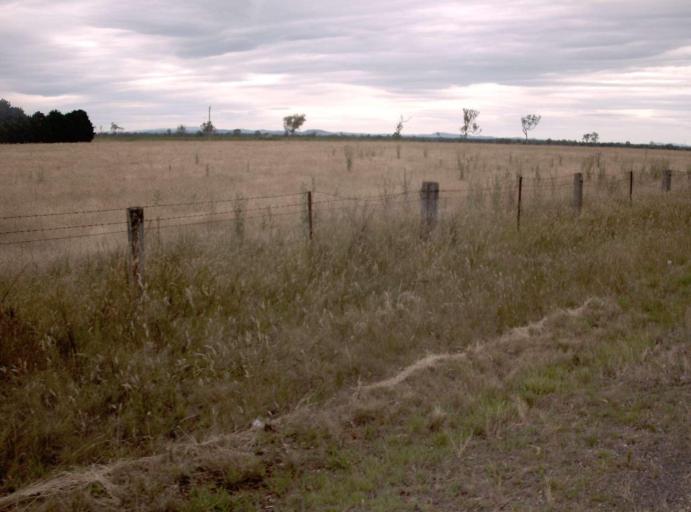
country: AU
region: Victoria
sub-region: East Gippsland
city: Bairnsdale
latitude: -37.9651
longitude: 147.4855
